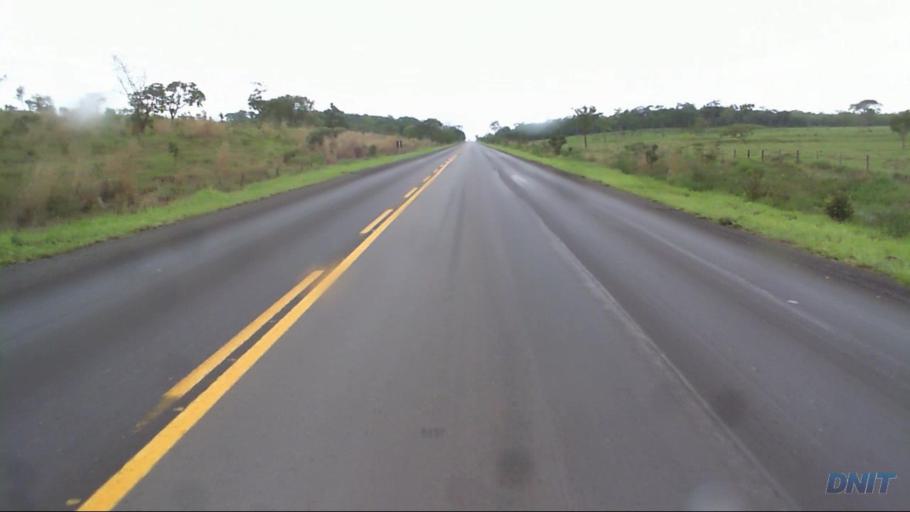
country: BR
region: Goias
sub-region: Padre Bernardo
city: Padre Bernardo
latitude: -15.2073
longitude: -48.4669
